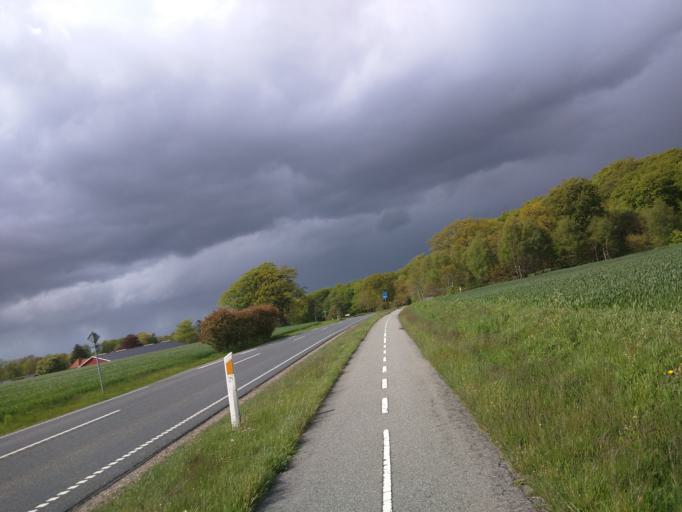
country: DK
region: Central Jutland
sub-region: Silkeborg Kommune
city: Kjellerup
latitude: 56.3192
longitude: 9.4201
